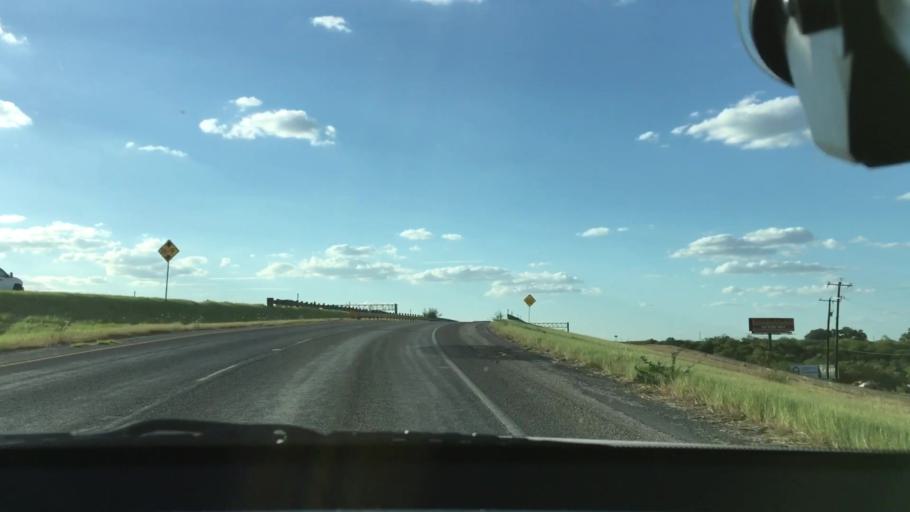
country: US
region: Texas
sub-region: Bexar County
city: Live Oak
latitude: 29.5804
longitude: -98.3436
